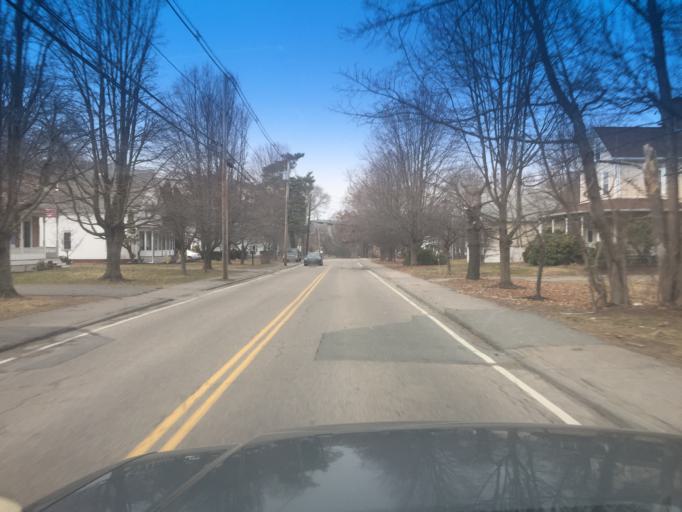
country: US
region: Massachusetts
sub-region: Norfolk County
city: Bellingham
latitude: 42.1181
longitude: -71.4519
